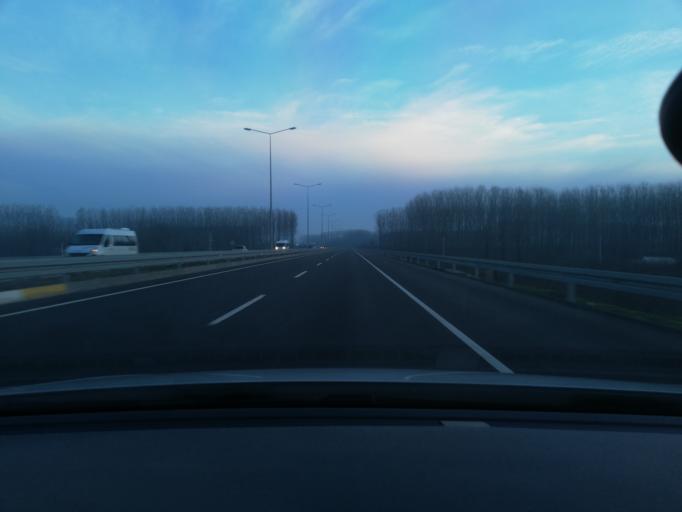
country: TR
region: Duzce
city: Duzce
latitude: 40.8063
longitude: 31.1686
